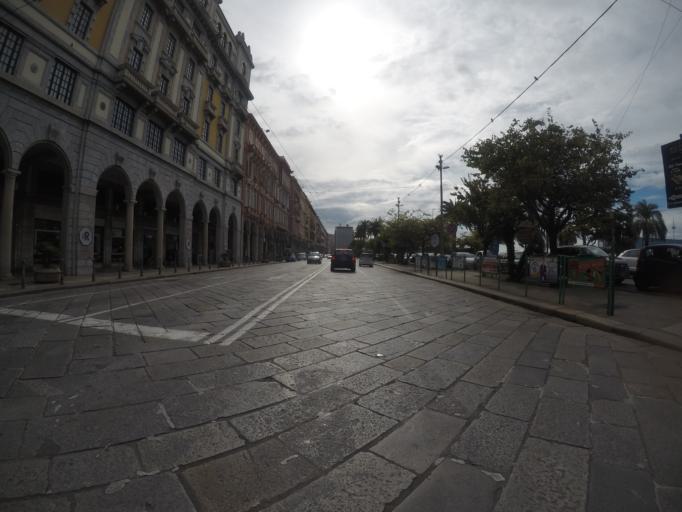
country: IT
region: Sardinia
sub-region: Provincia di Cagliari
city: Cagliari
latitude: 39.2147
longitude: 9.1110
